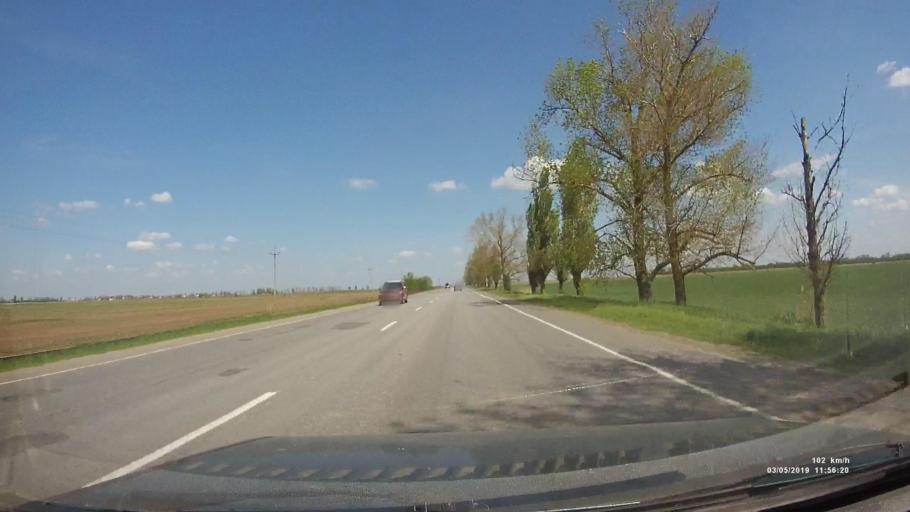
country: RU
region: Rostov
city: Bagayevskaya
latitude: 47.1933
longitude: 40.3000
